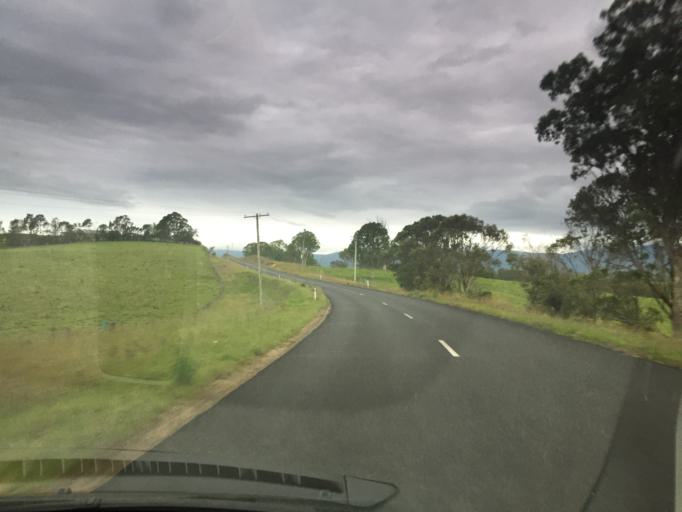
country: AU
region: New South Wales
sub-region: Bega Valley
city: Bega
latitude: -36.6474
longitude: 149.5842
